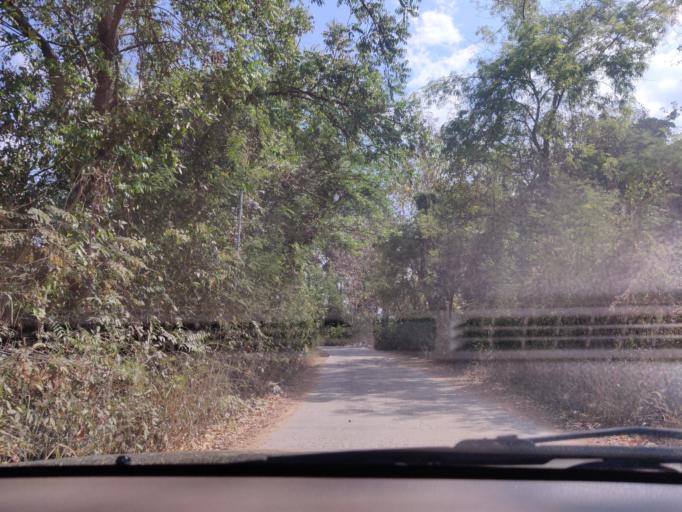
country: TH
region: Sisaket
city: Si Sa Ket
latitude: 15.0731
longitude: 104.3494
